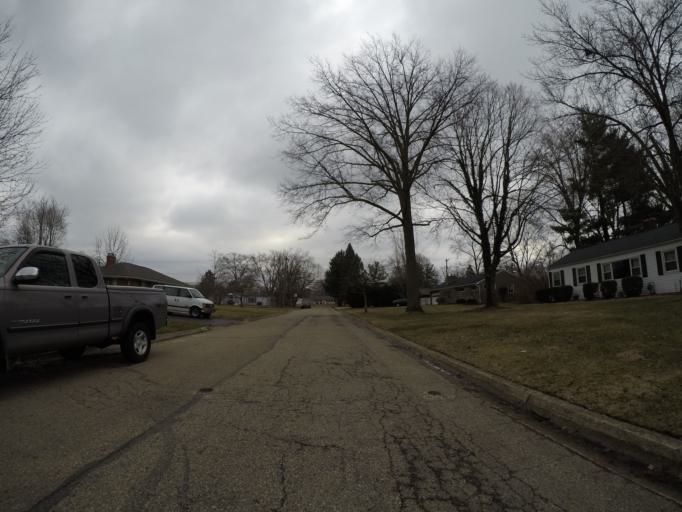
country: US
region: Ohio
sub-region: Franklin County
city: Upper Arlington
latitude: 40.0261
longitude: -83.0707
